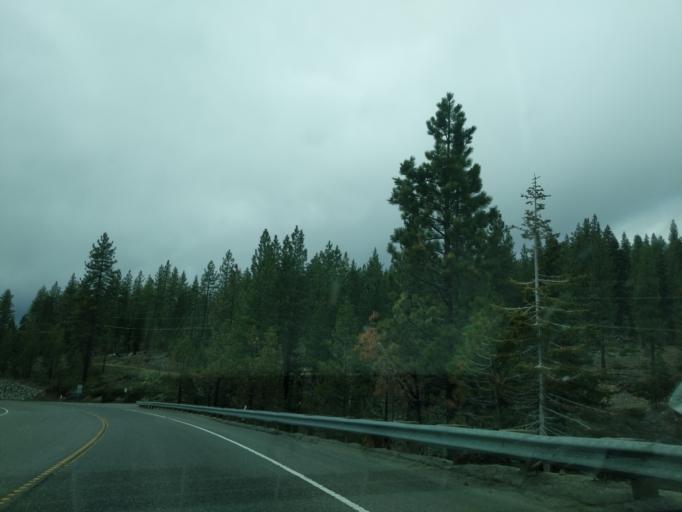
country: US
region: California
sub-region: Placer County
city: Tahoe Vista
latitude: 39.2670
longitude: -120.0734
